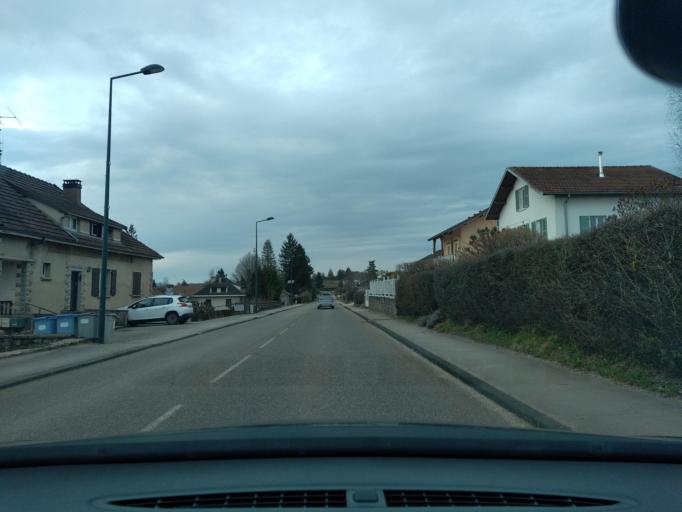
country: FR
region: Franche-Comte
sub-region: Departement du Jura
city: Orgelet
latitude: 46.5183
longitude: 5.6089
